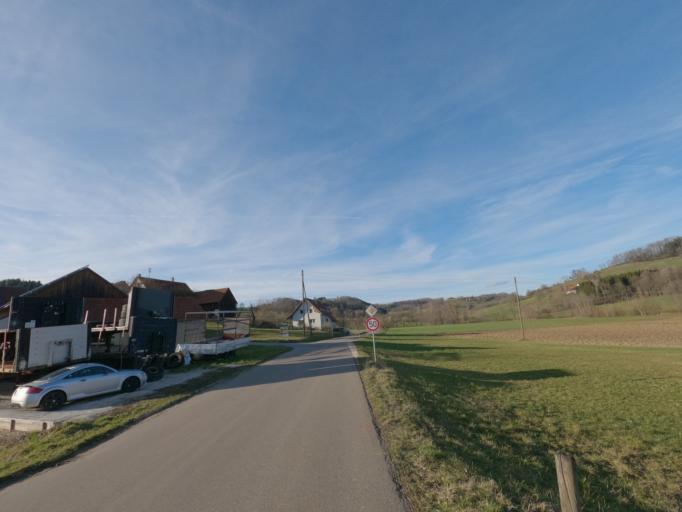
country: DE
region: Baden-Wuerttemberg
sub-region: Regierungsbezirk Stuttgart
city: Donzdorf
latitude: 48.7124
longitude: 9.7912
